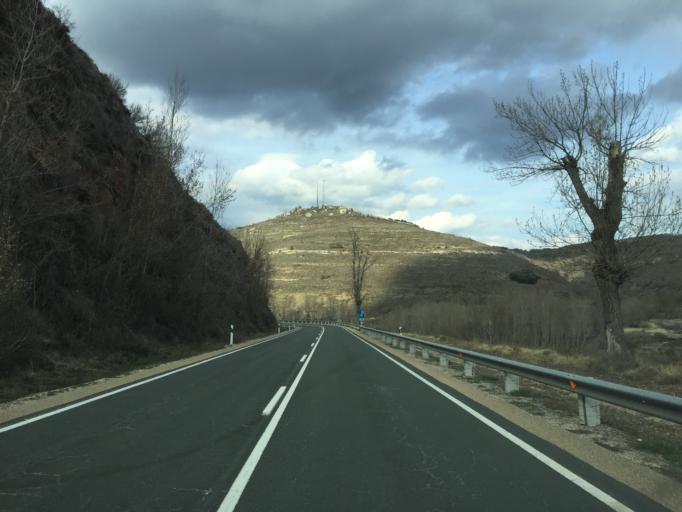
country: ES
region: Castille and Leon
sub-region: Provincia de Burgos
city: Tubilla del Agua
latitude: 42.7024
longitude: -3.8033
